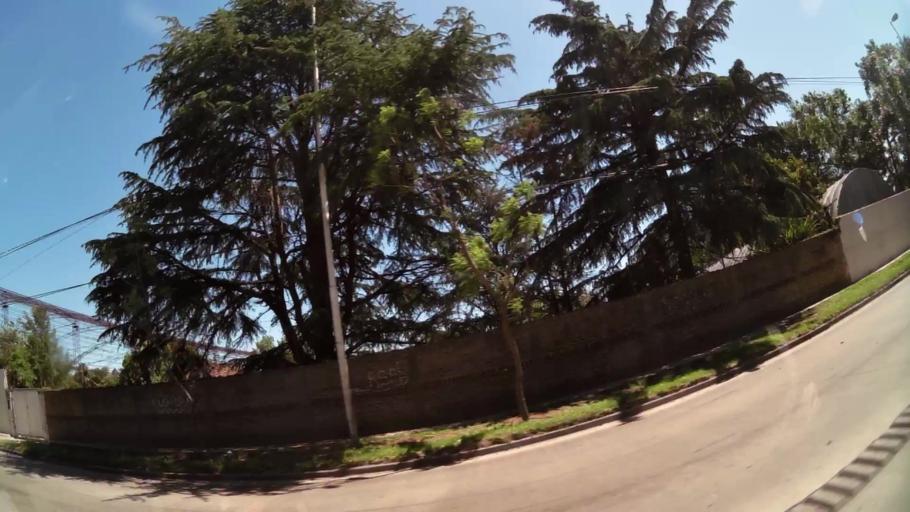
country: AR
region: Buenos Aires
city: Hurlingham
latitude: -34.4970
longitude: -58.6517
